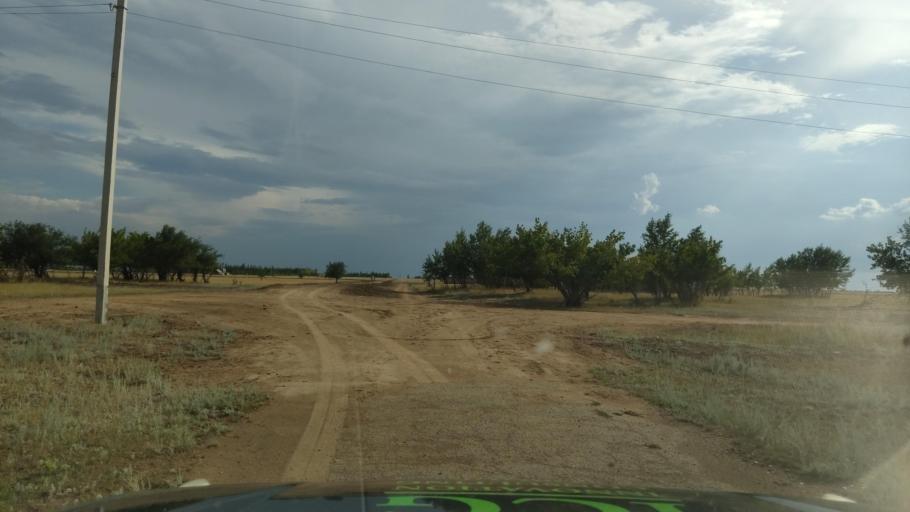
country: KZ
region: Pavlodar
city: Pavlodar
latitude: 52.5160
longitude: 77.4411
